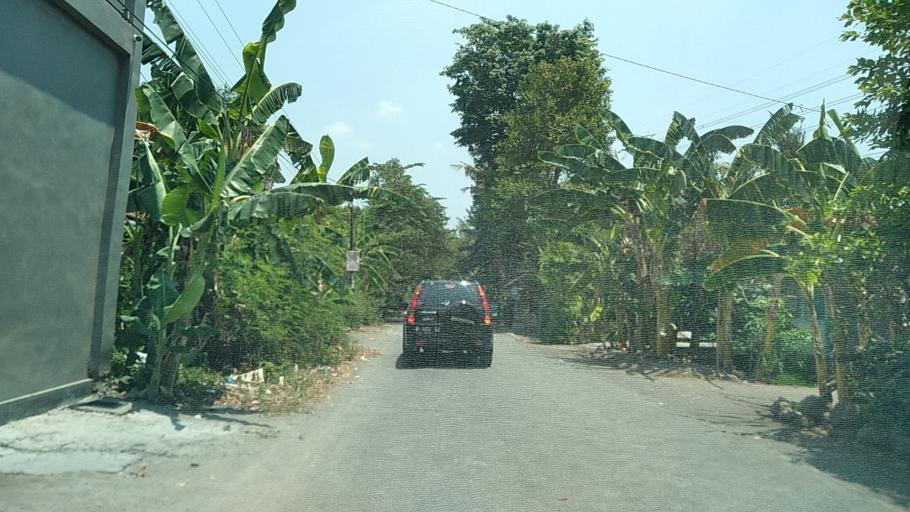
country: ID
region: Central Java
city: Mranggen
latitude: -7.0086
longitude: 110.4882
